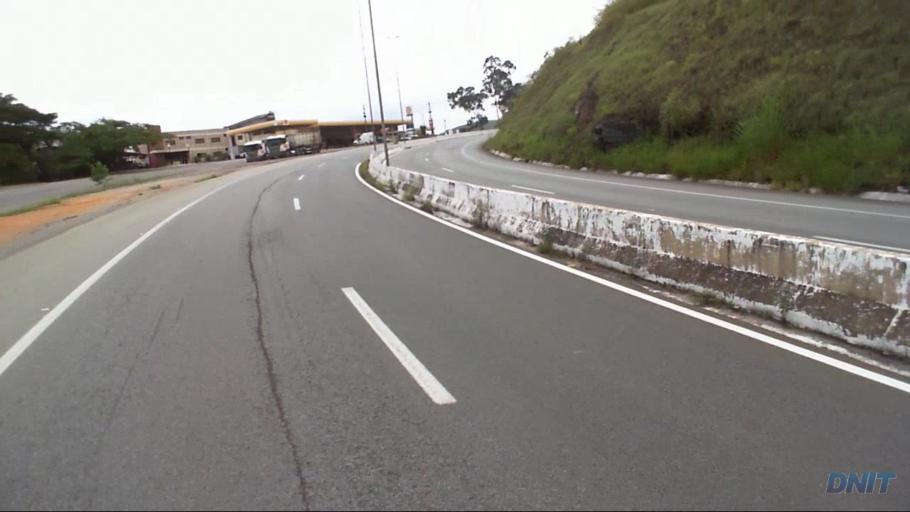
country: BR
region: Minas Gerais
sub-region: Nova Era
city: Nova Era
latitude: -19.7627
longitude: -43.0383
